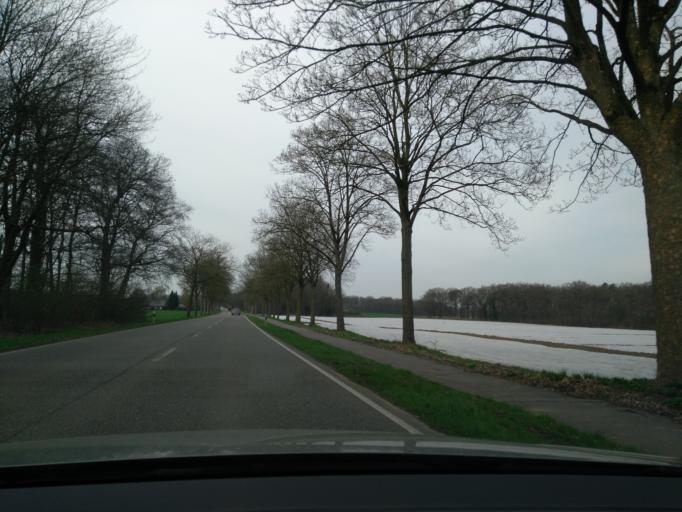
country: DE
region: North Rhine-Westphalia
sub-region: Regierungsbezirk Dusseldorf
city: Issum
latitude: 51.5869
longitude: 6.4243
